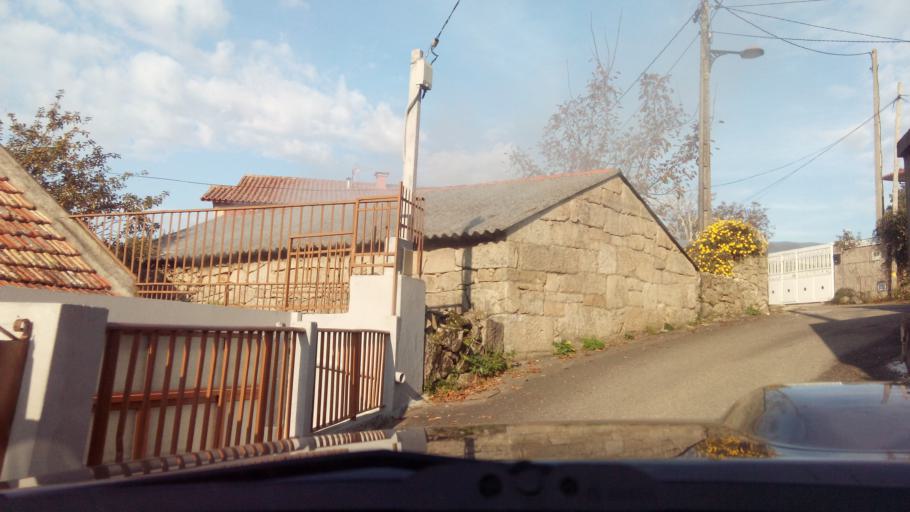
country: ES
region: Galicia
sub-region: Provincia de Pontevedra
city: Marin
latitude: 42.3640
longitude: -8.7343
